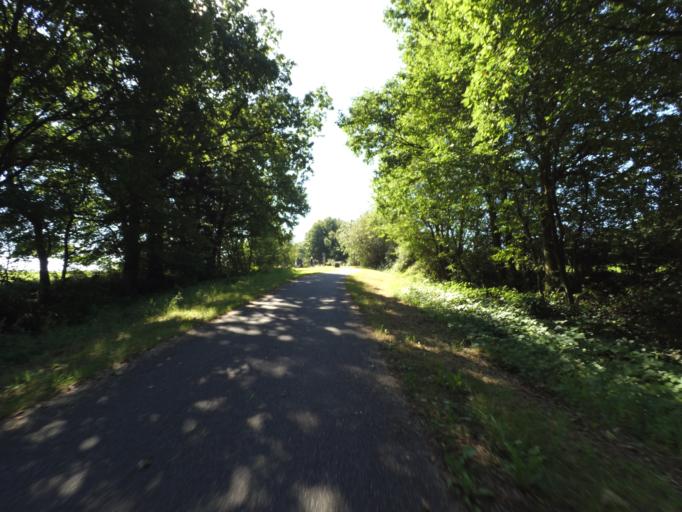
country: DE
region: Rheinland-Pfalz
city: Niederofflingen
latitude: 50.0673
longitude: 6.8933
